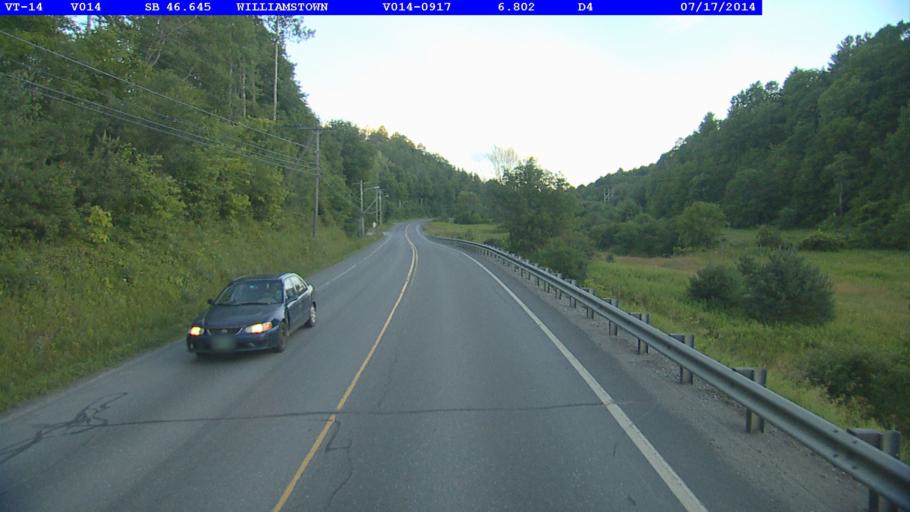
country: US
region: Vermont
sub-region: Washington County
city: South Barre
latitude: 44.1514
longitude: -72.5215
